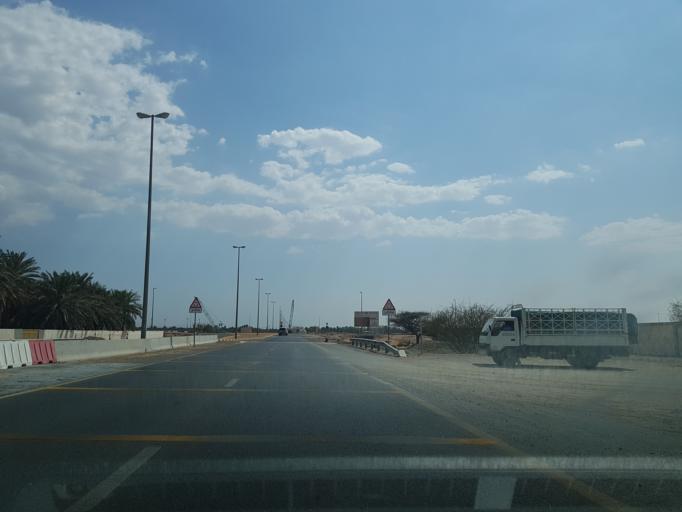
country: AE
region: Ash Shariqah
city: Adh Dhayd
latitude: 25.2346
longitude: 55.9167
